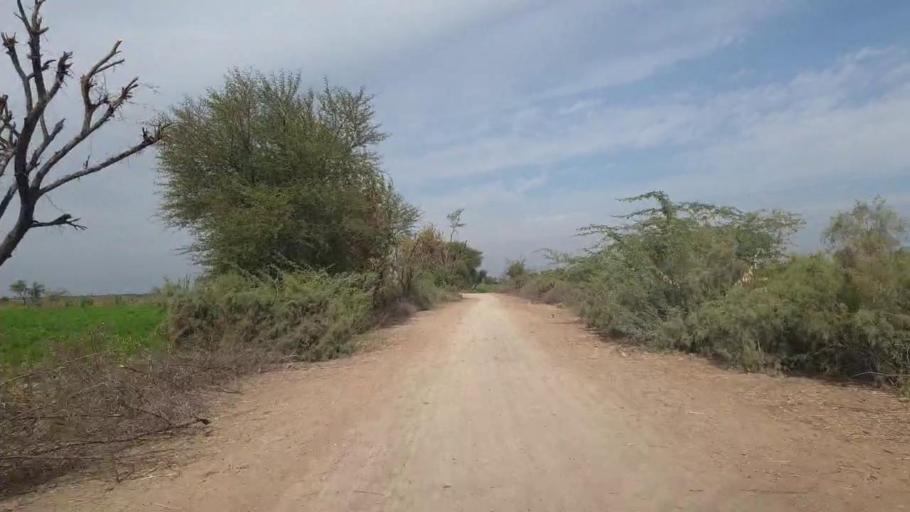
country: PK
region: Sindh
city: Sanghar
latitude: 26.0461
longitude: 68.9062
